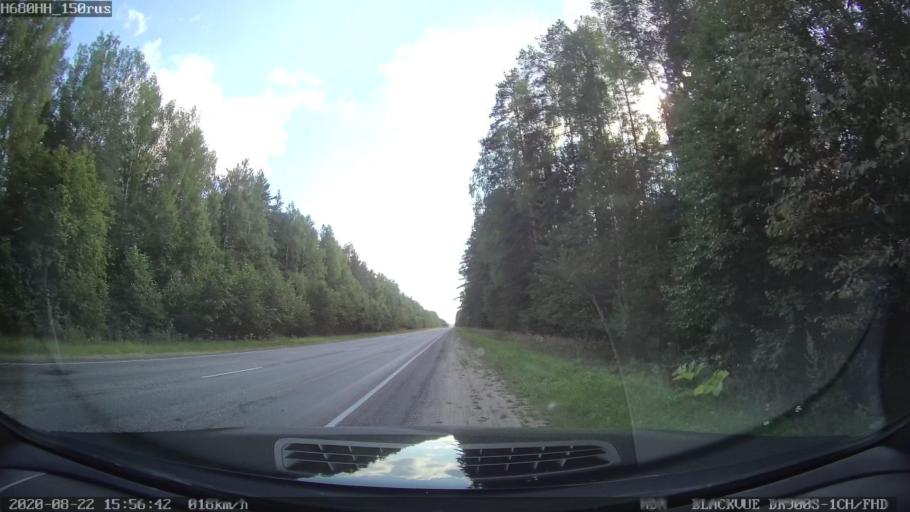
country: RU
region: Tverskaya
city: Bezhetsk
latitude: 57.6104
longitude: 36.3635
